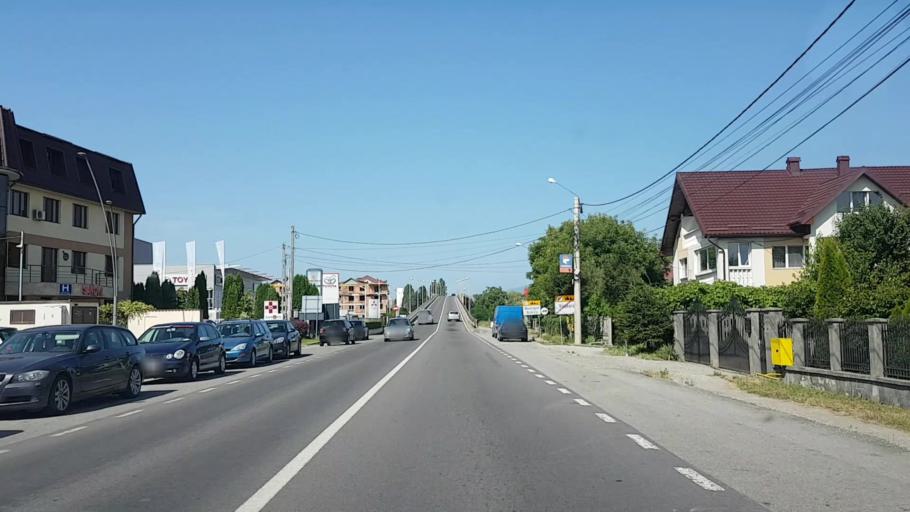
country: RO
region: Bistrita-Nasaud
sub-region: Municipiul Bistrita
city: Viisoara
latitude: 47.1141
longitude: 24.4630
